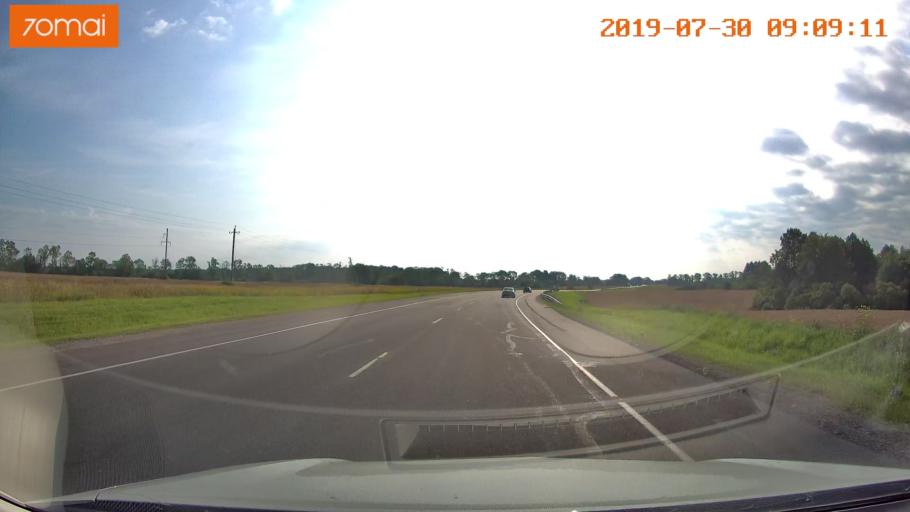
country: RU
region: Kaliningrad
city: Nesterov
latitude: 54.6138
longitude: 22.4040
